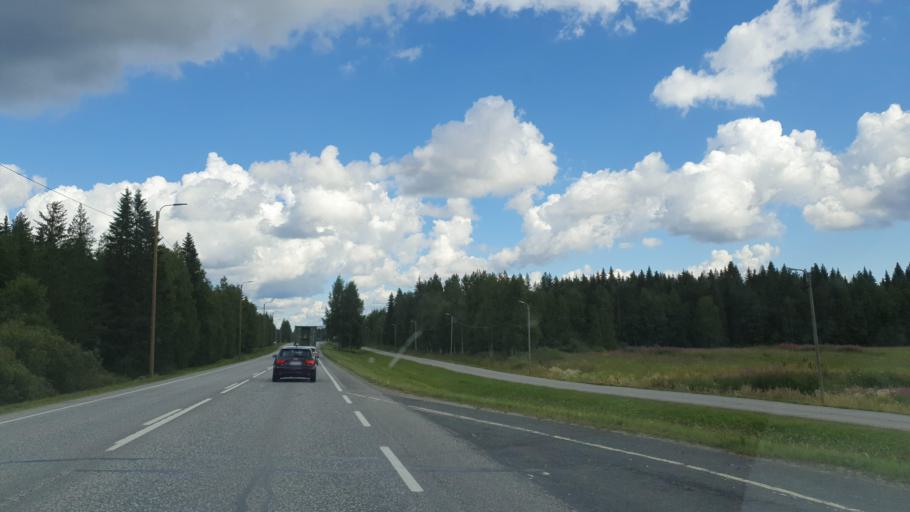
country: FI
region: Kainuu
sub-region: Kajaani
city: Kajaani
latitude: 64.2071
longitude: 27.6508
